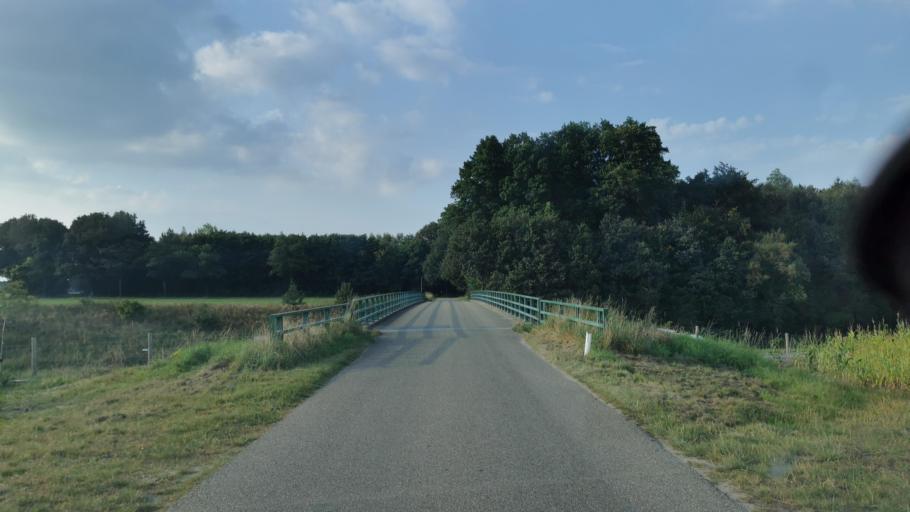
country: NL
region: Overijssel
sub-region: Gemeente Oldenzaal
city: Oldenzaal
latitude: 52.2930
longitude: 6.9549
